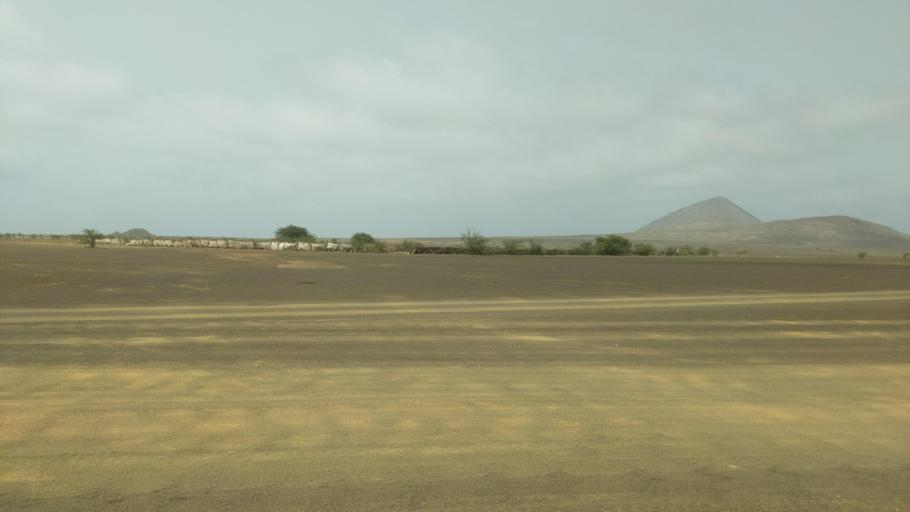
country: CV
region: Sal
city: Espargos
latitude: 16.7963
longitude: -22.9542
